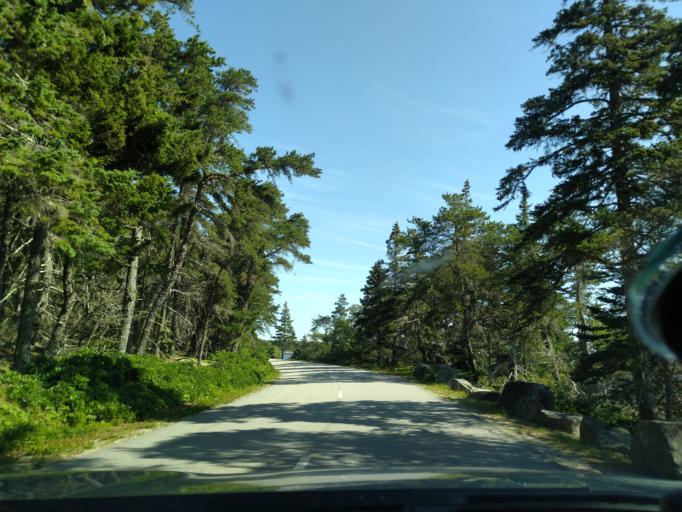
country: US
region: Maine
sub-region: Hancock County
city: Gouldsboro
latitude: 44.3492
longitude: -68.0462
